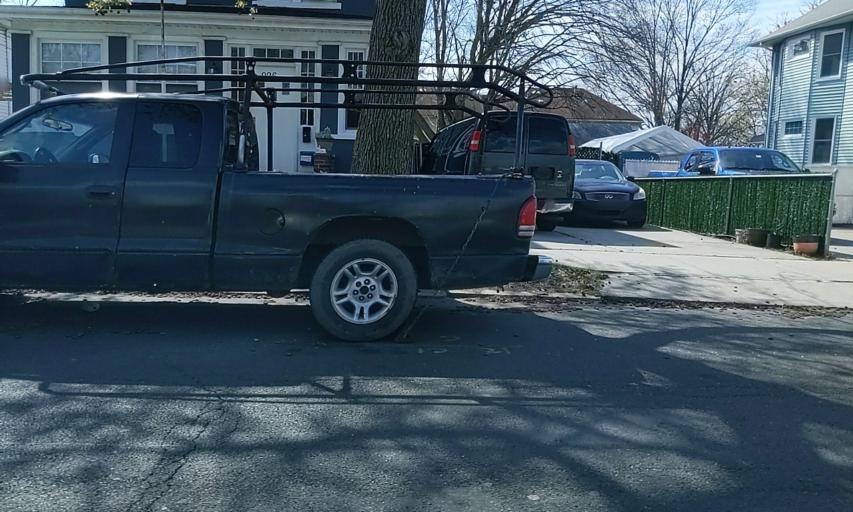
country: US
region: New York
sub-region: Richmond County
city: Bloomfield
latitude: 40.6136
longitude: -74.1308
